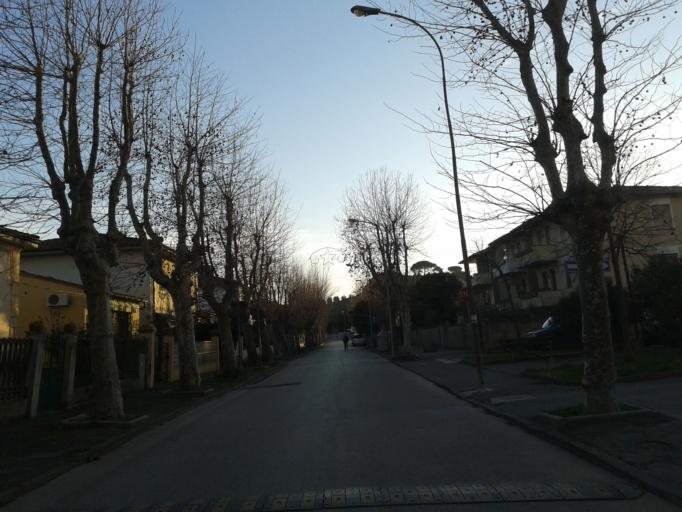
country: IT
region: Tuscany
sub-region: Provincia di Livorno
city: Guasticce
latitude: 43.5969
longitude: 10.4065
